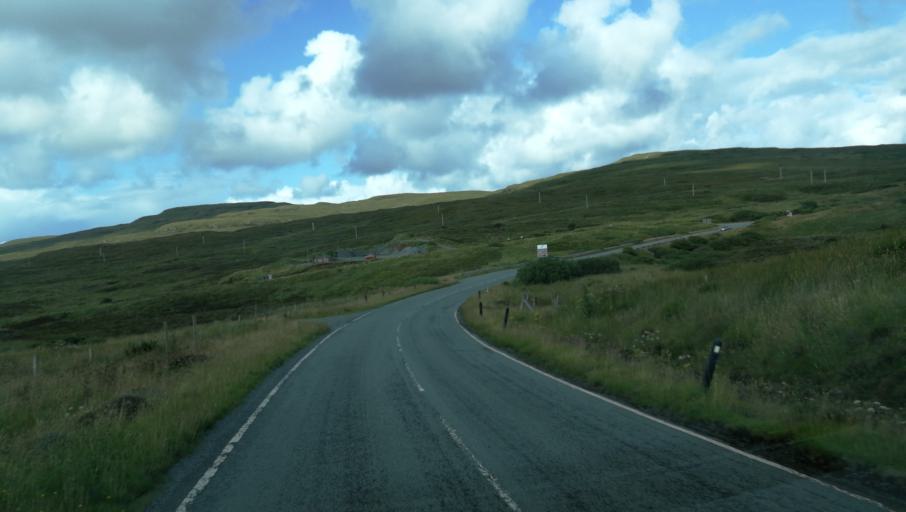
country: GB
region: Scotland
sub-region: Highland
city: Isle of Skye
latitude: 57.4684
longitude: -6.5411
